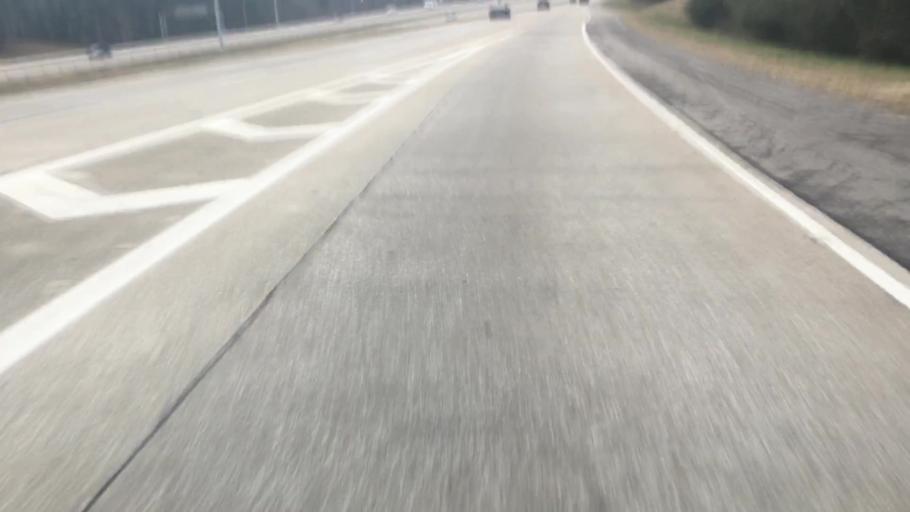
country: US
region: Alabama
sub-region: Jefferson County
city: Hoover
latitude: 33.3933
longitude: -86.7876
